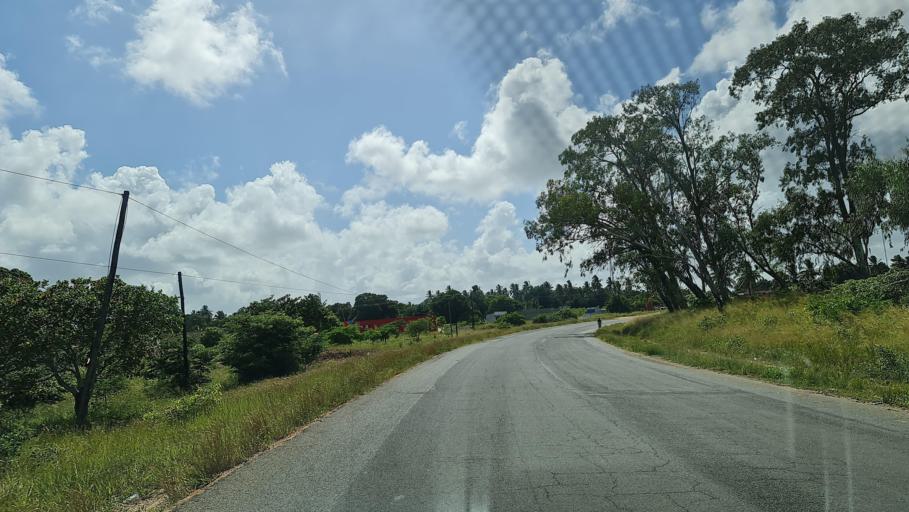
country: MZ
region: Gaza
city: Manjacaze
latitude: -24.6736
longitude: 34.5739
